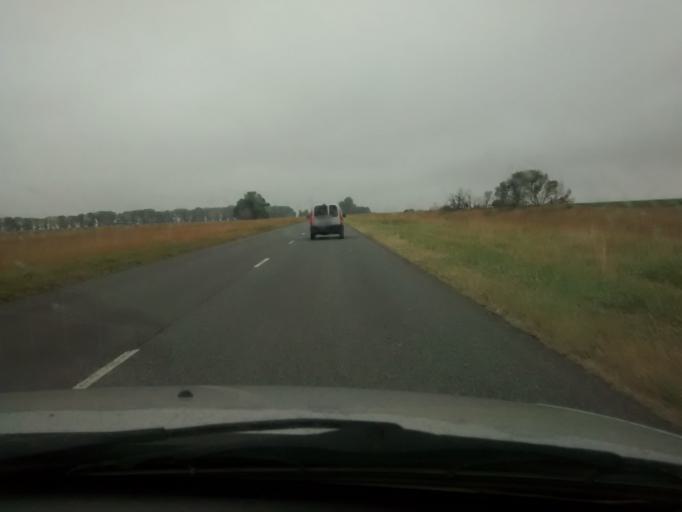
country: AR
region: Buenos Aires
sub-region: Partido de Ayacucho
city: Ayacucho
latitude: -37.4692
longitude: -58.4782
